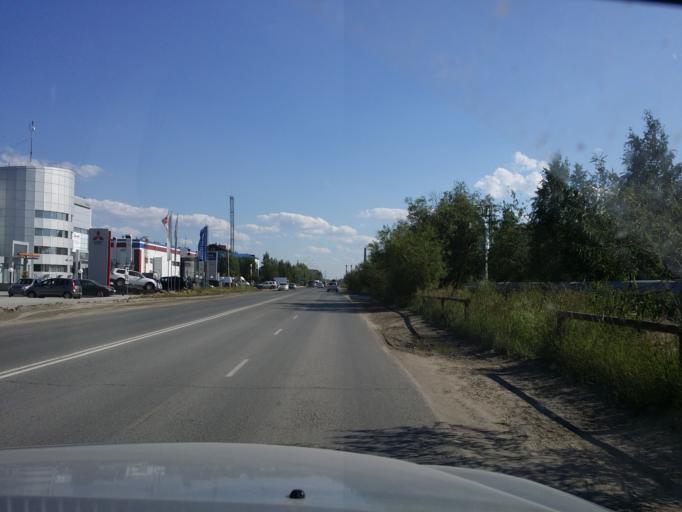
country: RU
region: Khanty-Mansiyskiy Avtonomnyy Okrug
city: Nizhnevartovsk
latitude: 60.9472
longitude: 76.5479
